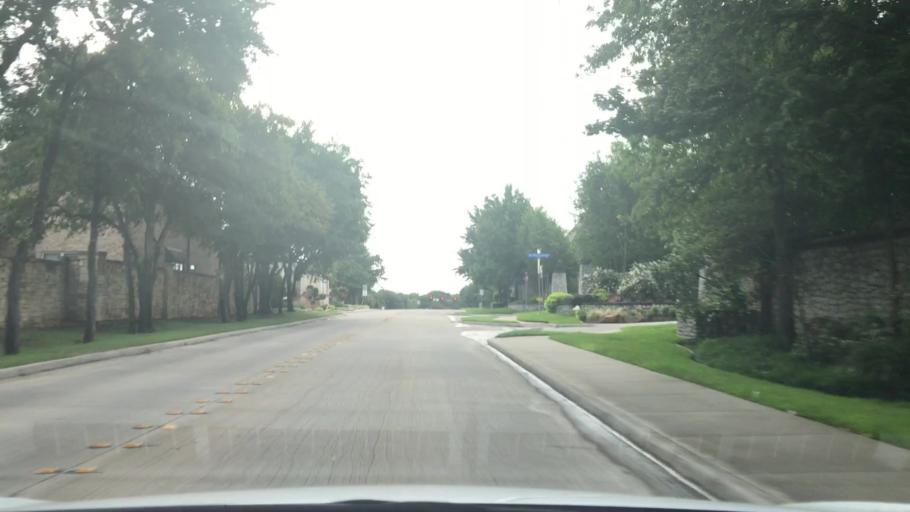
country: US
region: Texas
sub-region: Dallas County
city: Coppell
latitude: 32.9545
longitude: -96.9963
